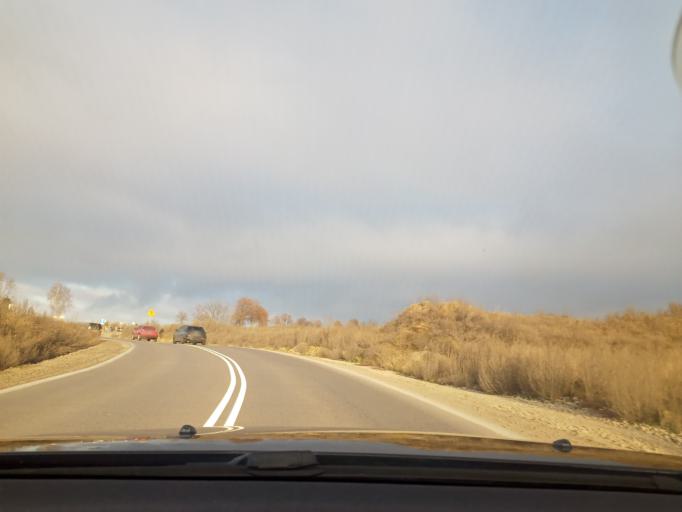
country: PL
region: Lesser Poland Voivodeship
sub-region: Powiat miechowski
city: Miechow
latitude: 50.3182
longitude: 20.0394
